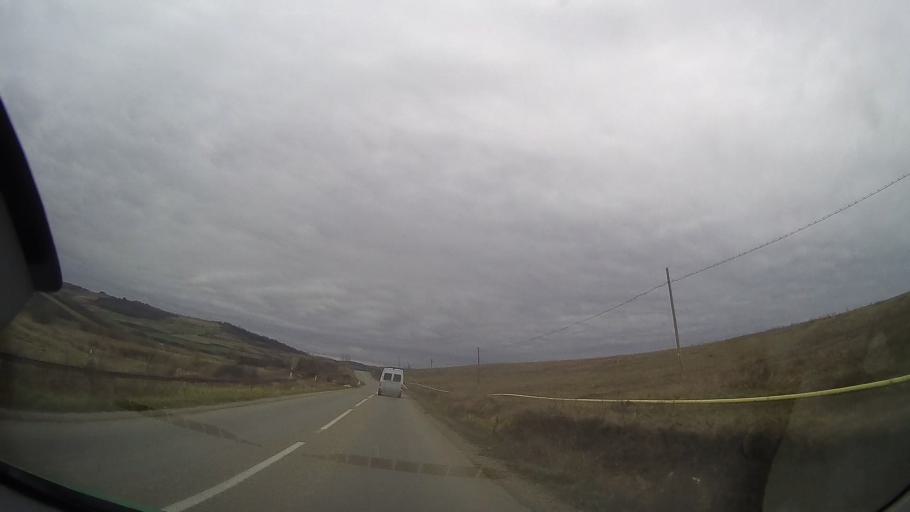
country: RO
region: Cluj
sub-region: Comuna Catina
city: Catina
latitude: 46.8037
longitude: 24.2142
